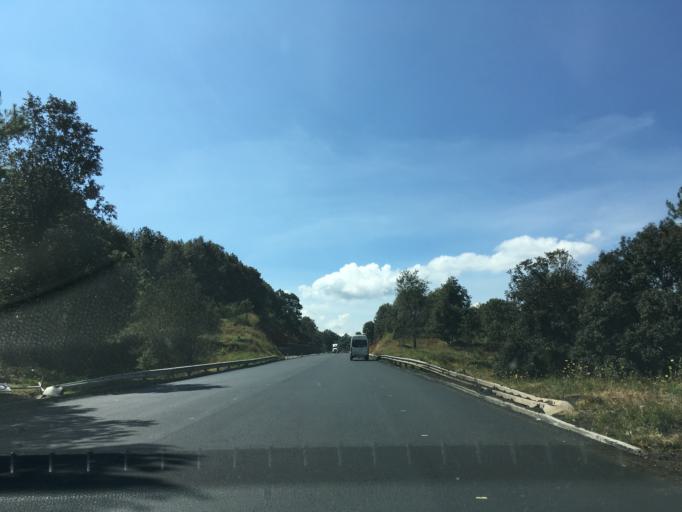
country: MX
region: Michoacan
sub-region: Patzcuaro
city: Santa Ana Chapitiro
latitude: 19.5054
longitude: -101.6827
